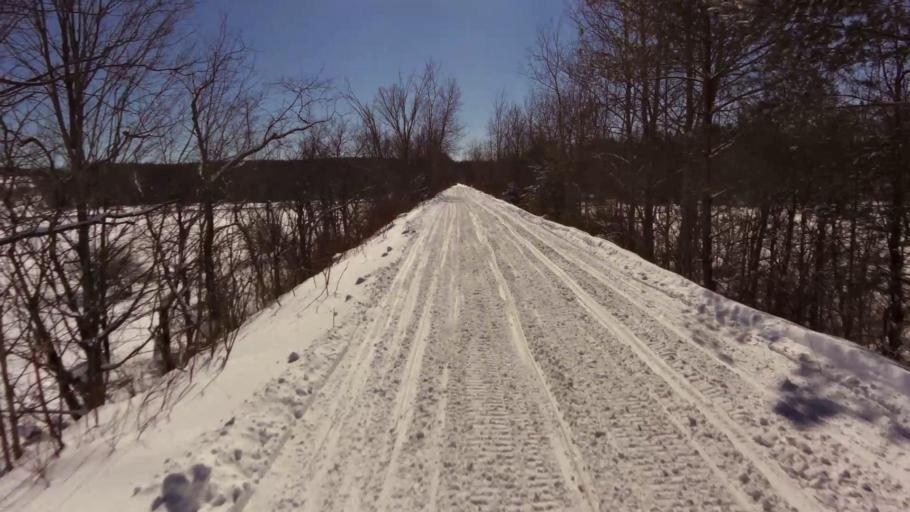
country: US
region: New York
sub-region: Chautauqua County
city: Mayville
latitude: 42.1615
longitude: -79.5854
